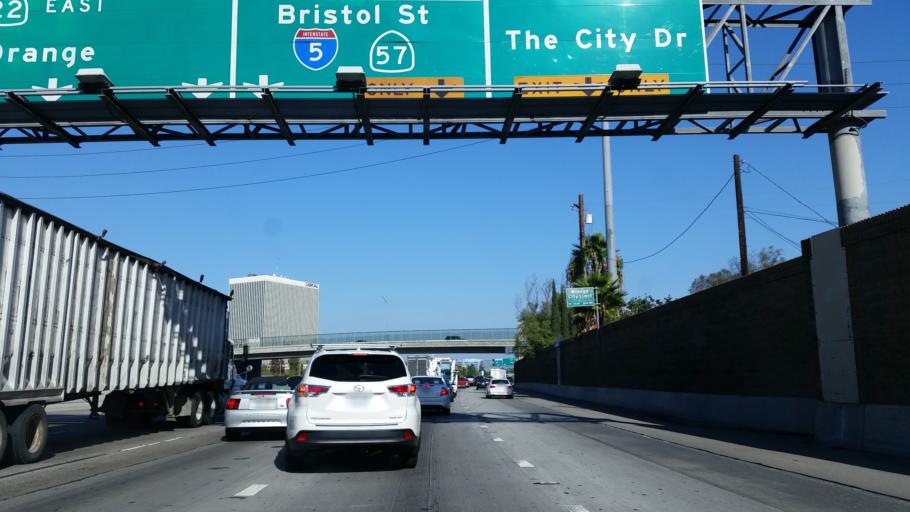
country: US
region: California
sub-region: Orange County
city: Garden Grove
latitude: 33.7777
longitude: -117.8980
